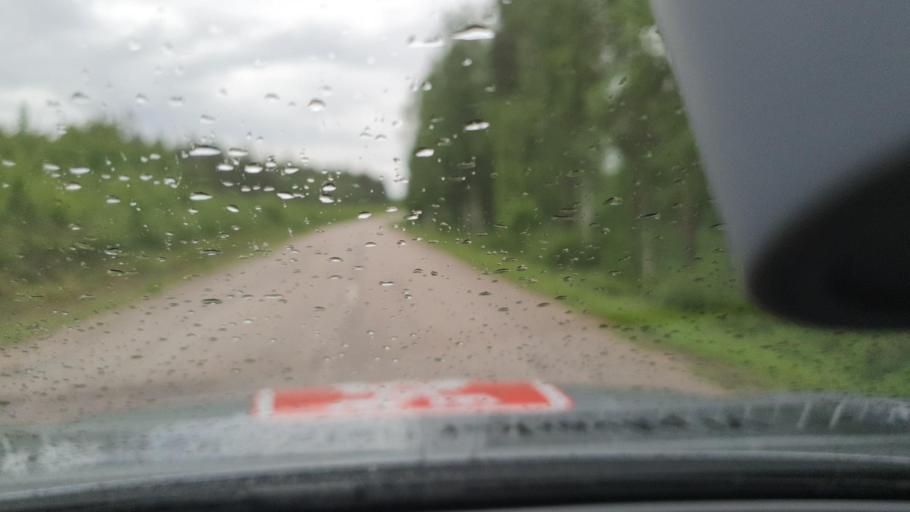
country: SE
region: Norrbotten
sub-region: Overkalix Kommun
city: OEverkalix
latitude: 66.4032
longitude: 22.7879
